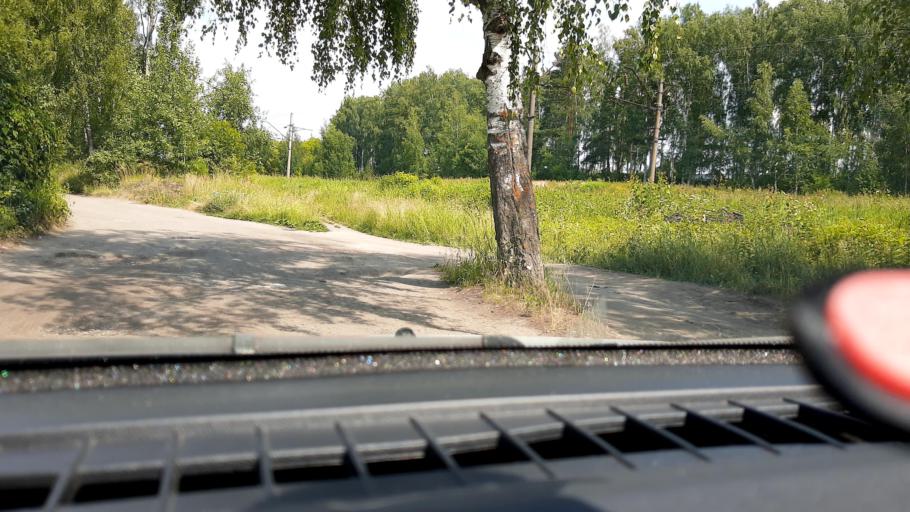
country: RU
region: Nizjnij Novgorod
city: Neklyudovo
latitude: 56.4477
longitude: 44.0036
